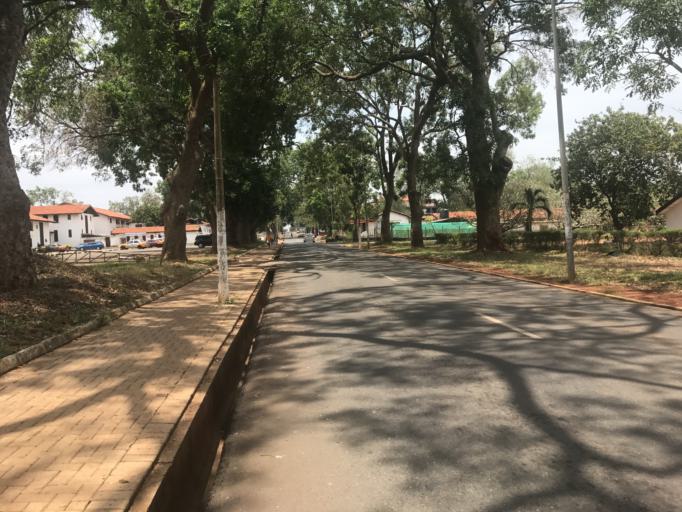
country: GH
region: Greater Accra
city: Medina Estates
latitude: 5.6488
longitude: -0.1850
